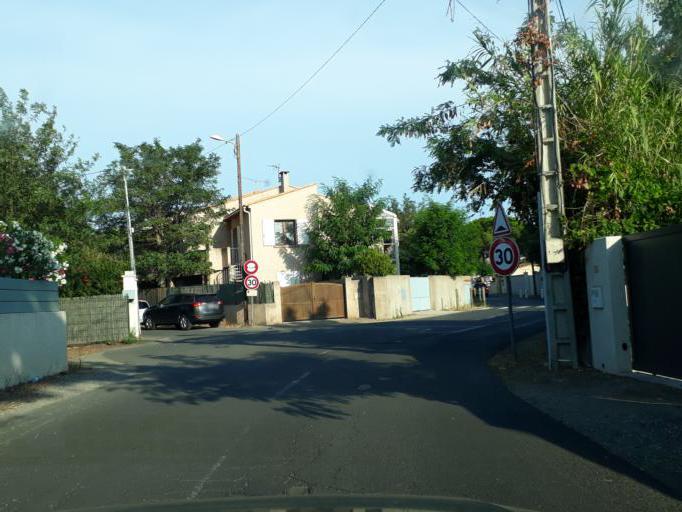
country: FR
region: Languedoc-Roussillon
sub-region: Departement de l'Herault
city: Agde
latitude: 43.2833
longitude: 3.4553
